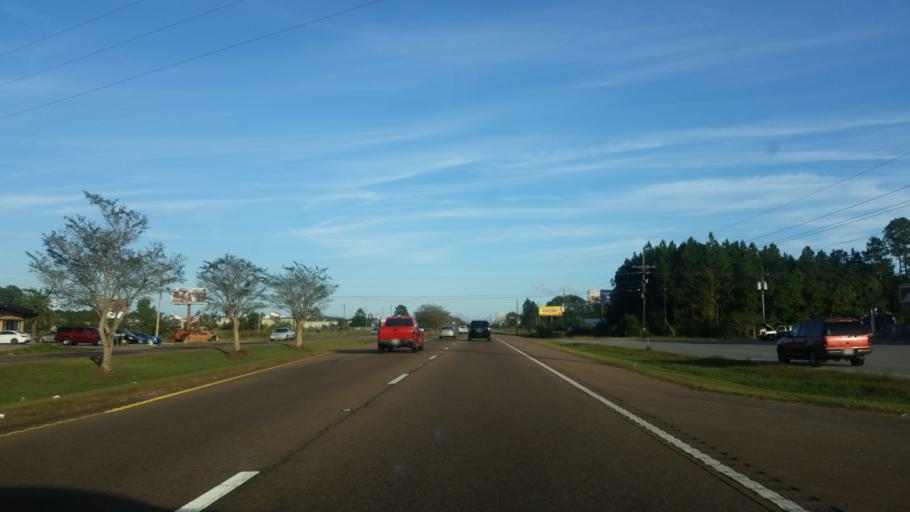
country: US
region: Mississippi
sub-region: Jackson County
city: Gautier
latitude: 30.3945
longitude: -88.6690
